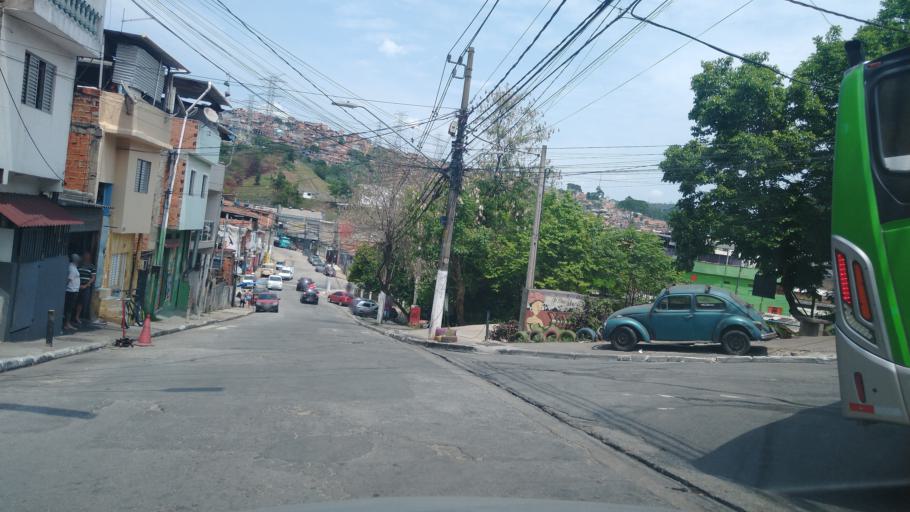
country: BR
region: Sao Paulo
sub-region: Caieiras
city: Caieiras
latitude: -23.4514
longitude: -46.6976
